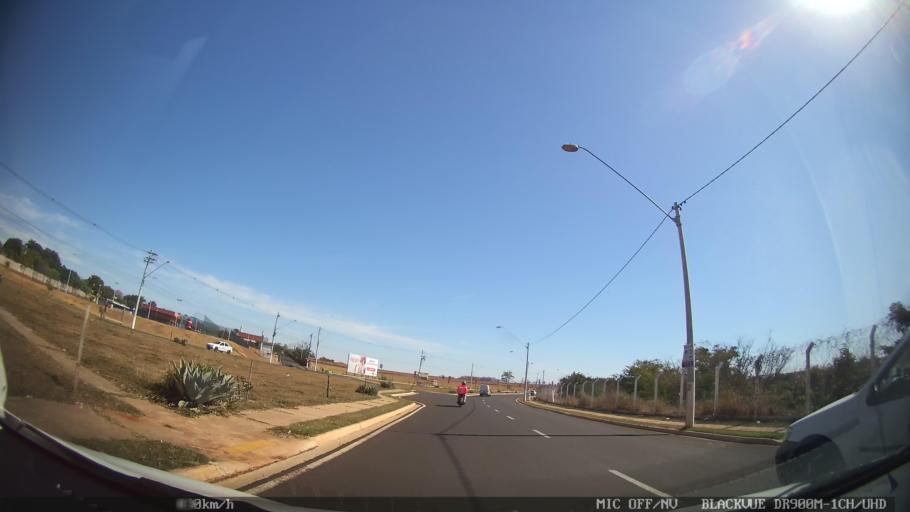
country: BR
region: Sao Paulo
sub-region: Sao Jose Do Rio Preto
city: Sao Jose do Rio Preto
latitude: -20.7584
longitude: -49.4363
